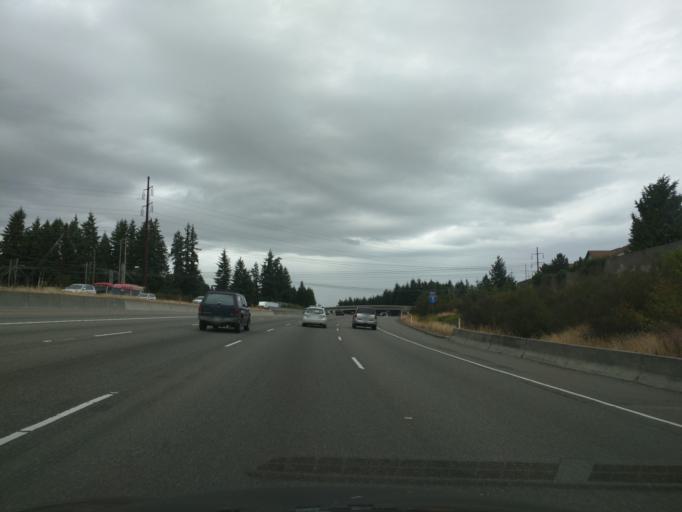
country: US
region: Washington
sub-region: Snohomish County
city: Everett
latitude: 47.9271
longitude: -122.2021
